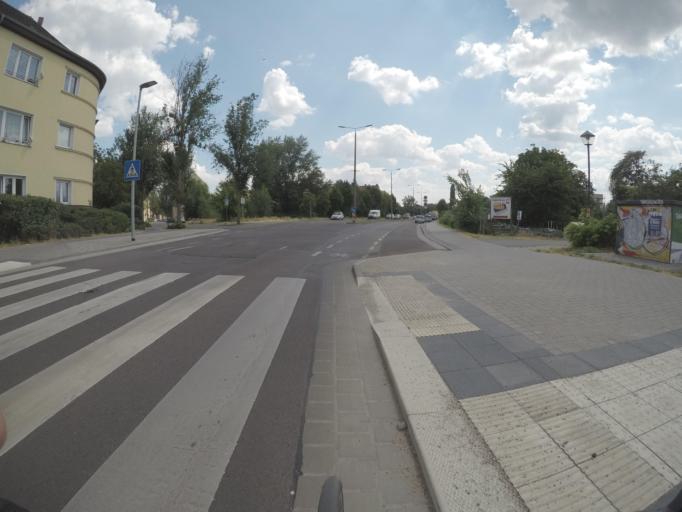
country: DE
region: Brandenburg
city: Brandenburg an der Havel
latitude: 52.4024
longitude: 12.5584
